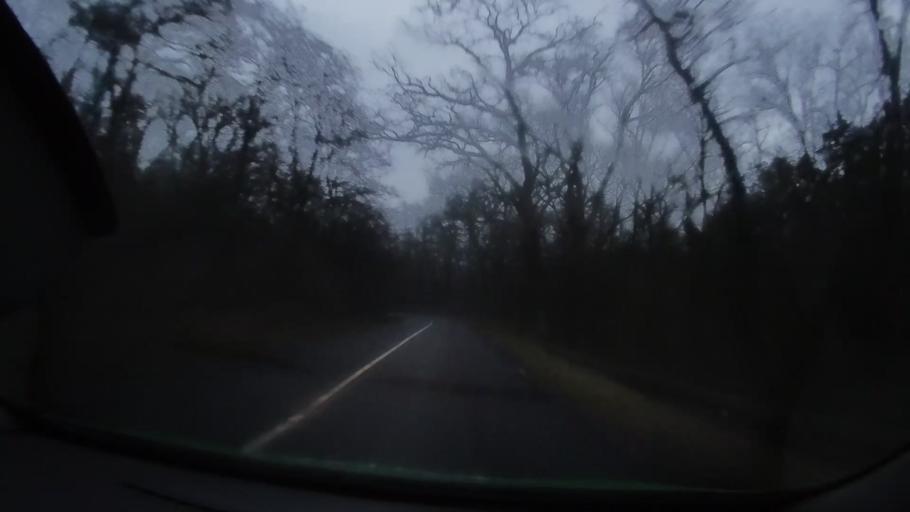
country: RO
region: Mures
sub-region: Comuna Solovastru
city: Solovastru
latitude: 46.7703
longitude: 24.7428
